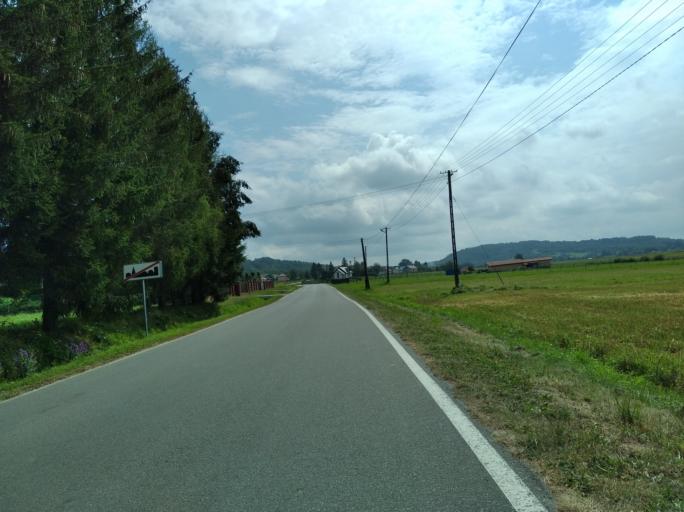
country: PL
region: Subcarpathian Voivodeship
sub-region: Powiat krosnienski
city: Wojaszowka
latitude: 49.7973
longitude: 21.6788
